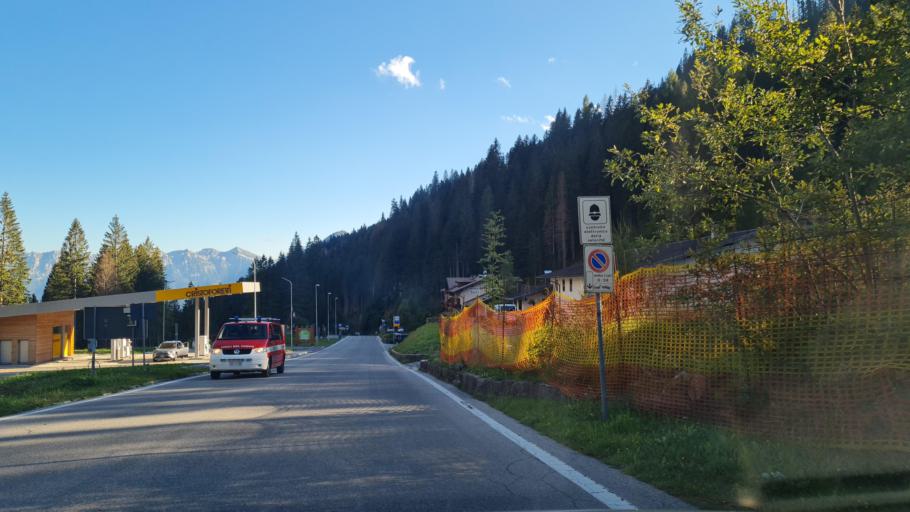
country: IT
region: Trentino-Alto Adige
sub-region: Provincia di Trento
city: Siror
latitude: 46.2536
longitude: 11.8026
